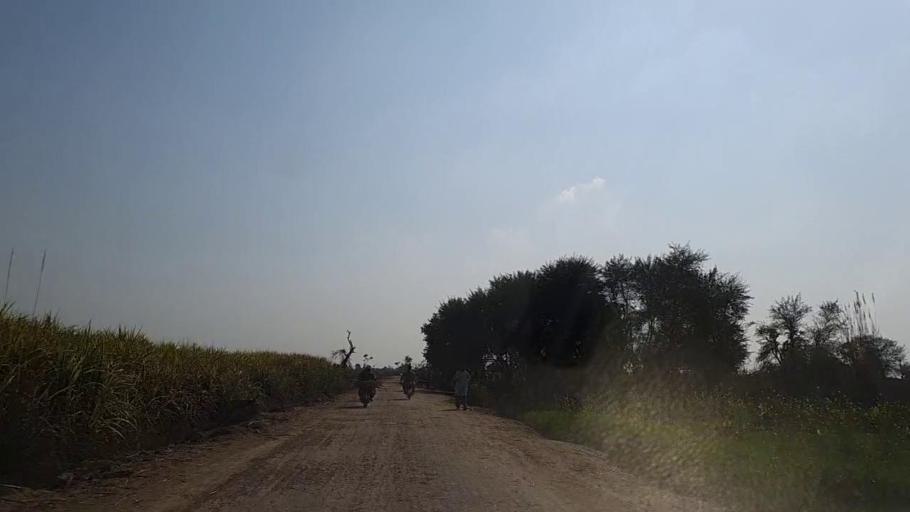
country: PK
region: Sindh
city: Daur
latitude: 26.4194
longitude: 68.2367
